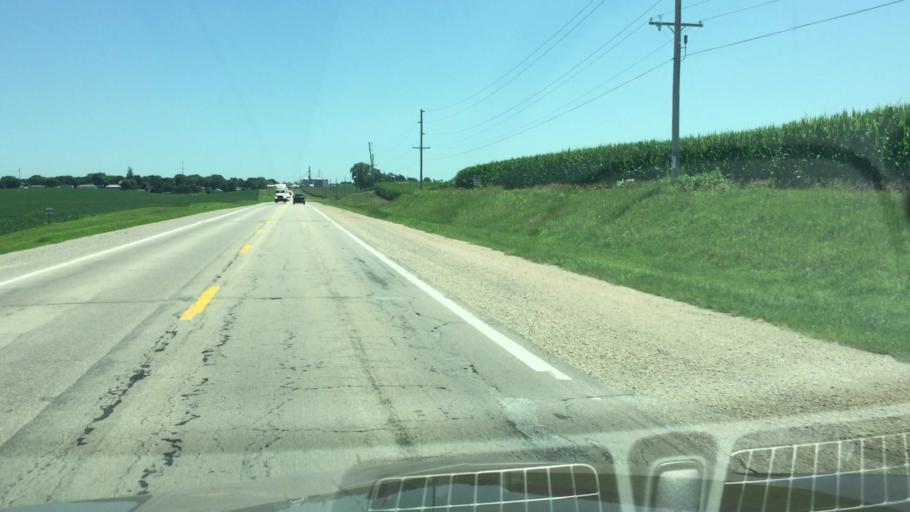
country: US
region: Iowa
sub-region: Cedar County
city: Mechanicsville
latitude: 41.8885
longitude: -91.1715
